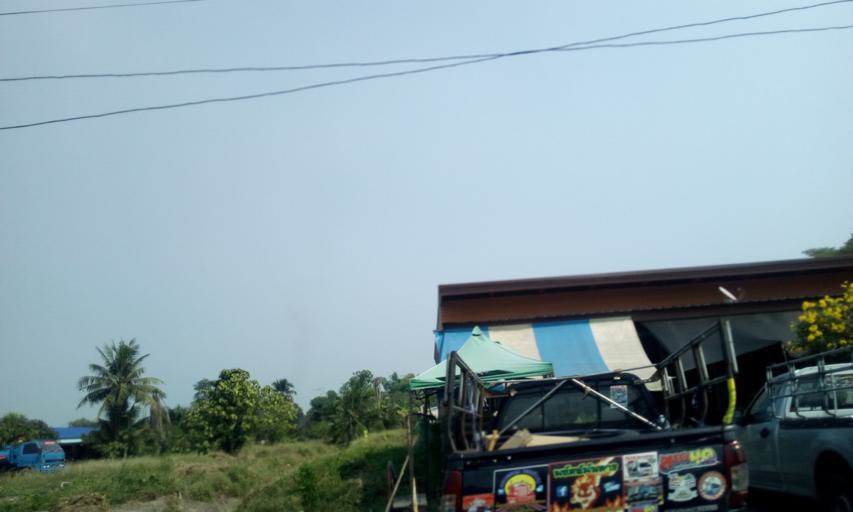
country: TH
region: Pathum Thani
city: Lam Luk Ka
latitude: 13.9604
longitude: 100.7253
